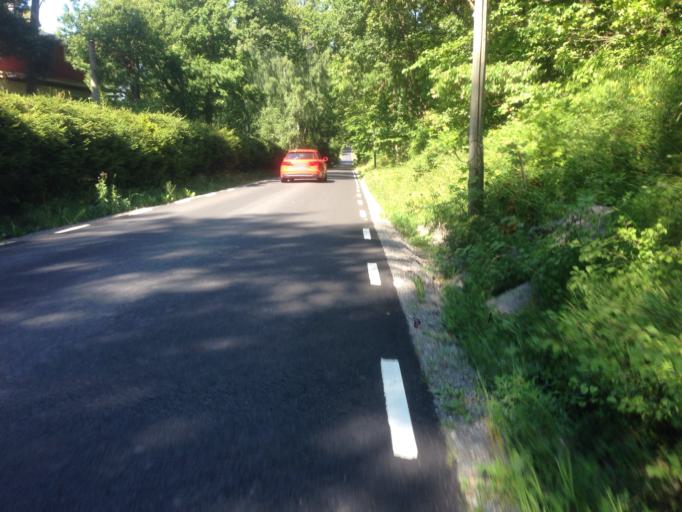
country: SE
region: Stockholm
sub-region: Vaxholms Kommun
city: Vaxholm
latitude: 59.3801
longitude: 18.3761
